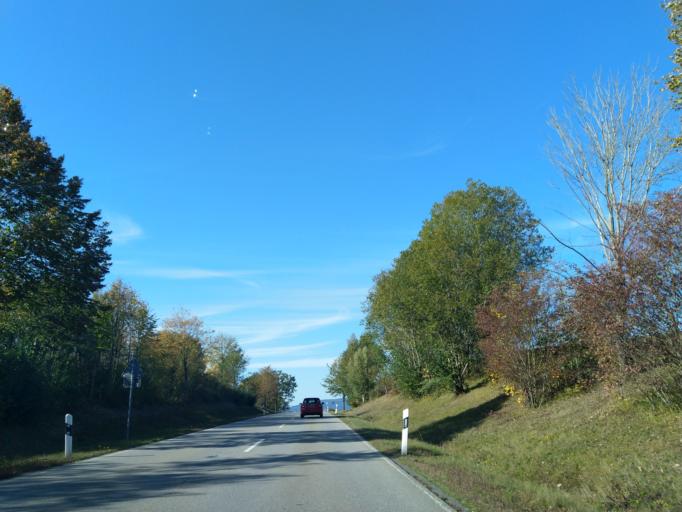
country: DE
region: Bavaria
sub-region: Lower Bavaria
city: Metten
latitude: 48.8607
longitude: 12.9389
